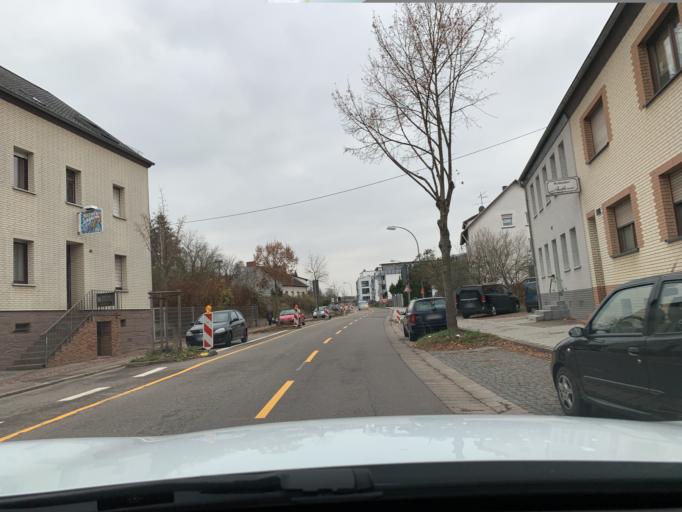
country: DE
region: Saarland
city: Kleinblittersdorf
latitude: 49.1778
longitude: 7.0369
